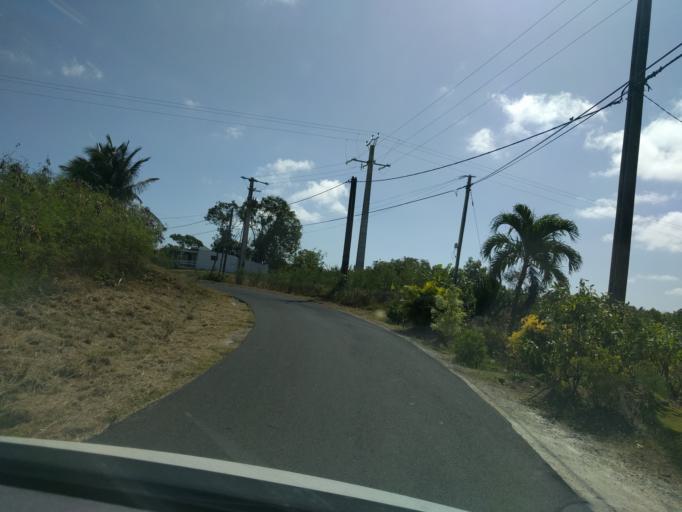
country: GP
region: Guadeloupe
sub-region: Guadeloupe
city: Grand-Bourg
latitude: 15.9775
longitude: -61.2479
